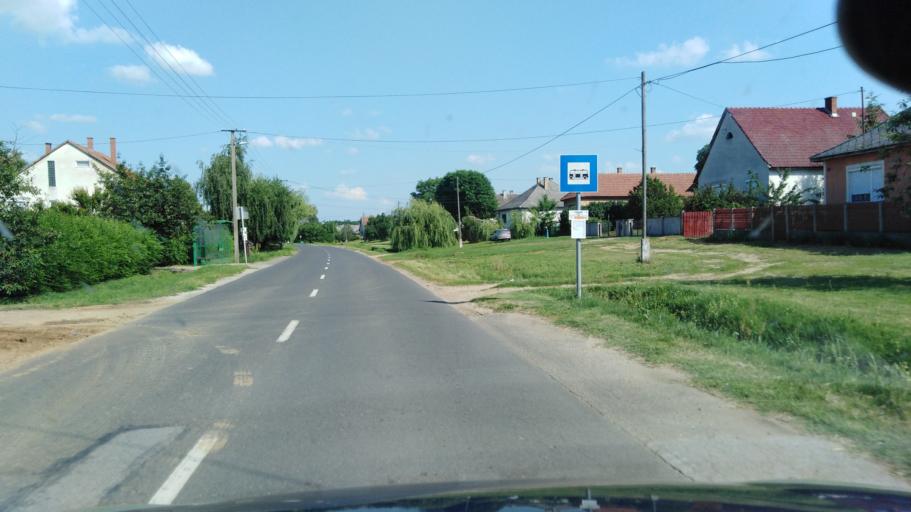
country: HU
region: Szabolcs-Szatmar-Bereg
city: Nyirvasvari
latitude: 47.8150
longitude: 22.1954
